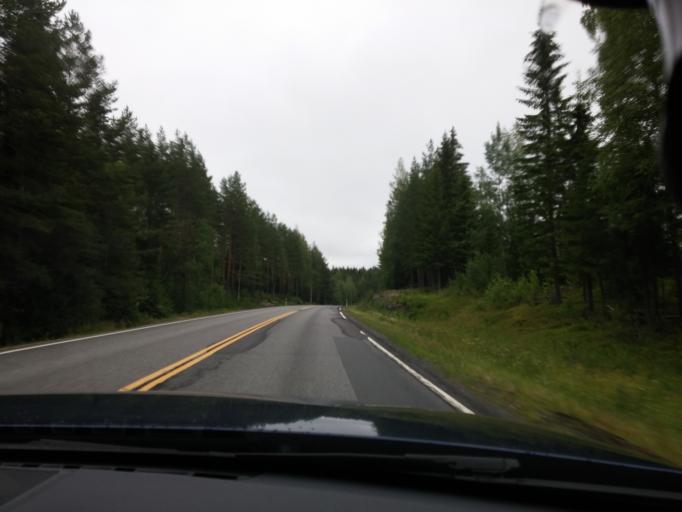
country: FI
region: Pirkanmaa
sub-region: Ylae-Pirkanmaa
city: Vilppula
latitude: 61.9532
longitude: 24.5516
